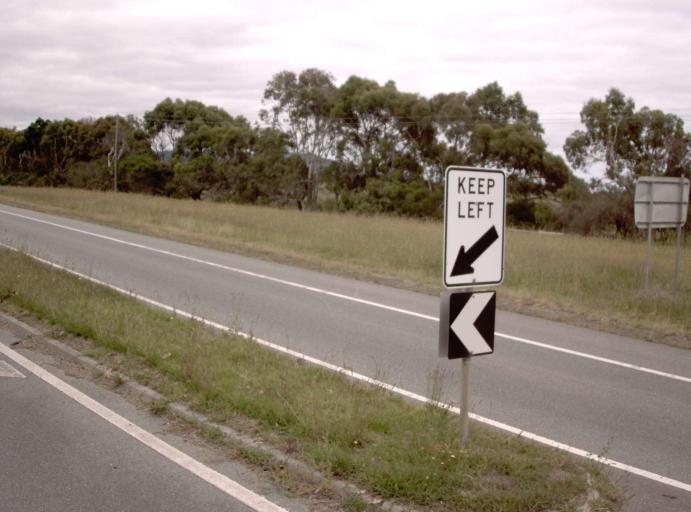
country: AU
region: Victoria
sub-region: Mornington Peninsula
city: Safety Beach
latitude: -38.3064
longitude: 145.0309
